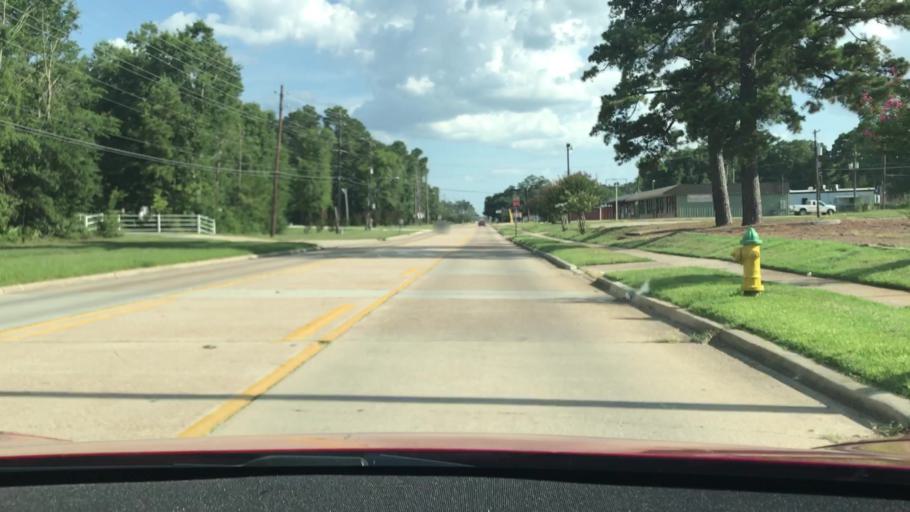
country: US
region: Louisiana
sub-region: Bossier Parish
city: Bossier City
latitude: 32.4100
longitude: -93.7804
